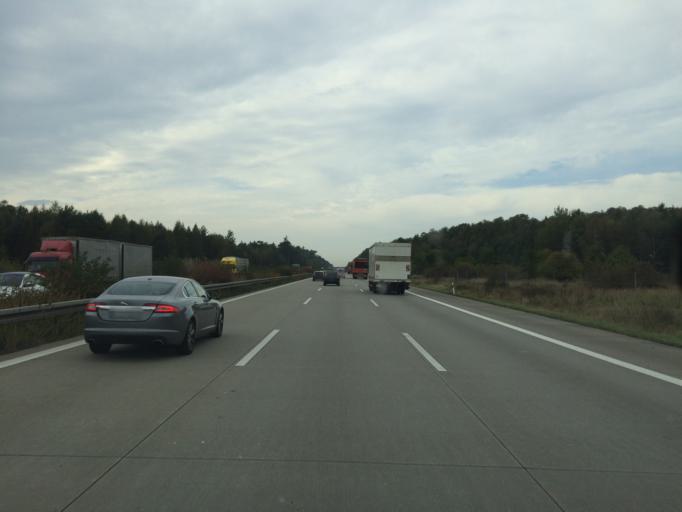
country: DE
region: Saxony-Anhalt
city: Tucheim
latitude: 52.2410
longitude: 12.1211
